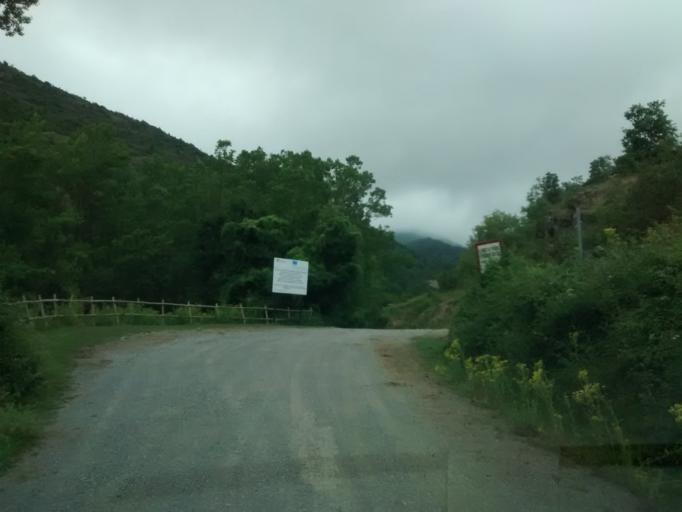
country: ES
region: La Rioja
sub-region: Provincia de La Rioja
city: Ajamil
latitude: 42.1609
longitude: -2.4851
